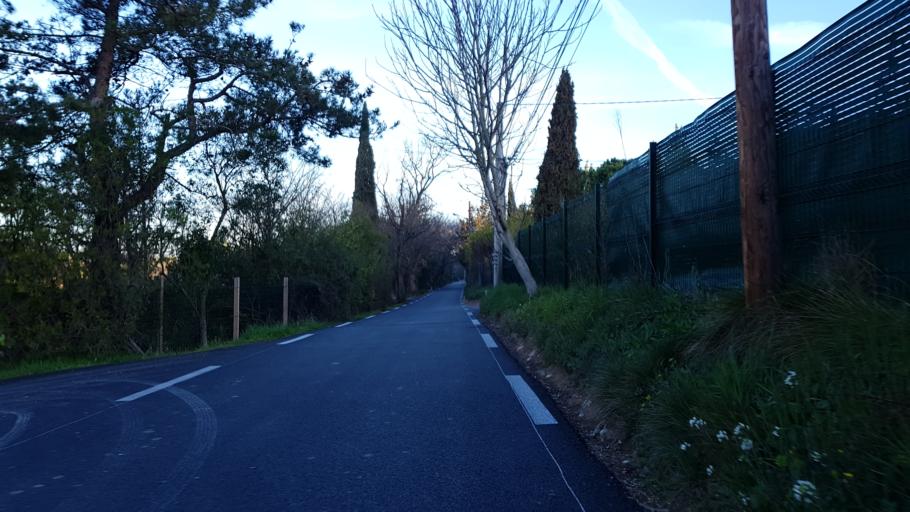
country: FR
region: Provence-Alpes-Cote d'Azur
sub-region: Departement des Bouches-du-Rhone
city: Bouc-Bel-Air
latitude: 43.4930
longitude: 5.4121
